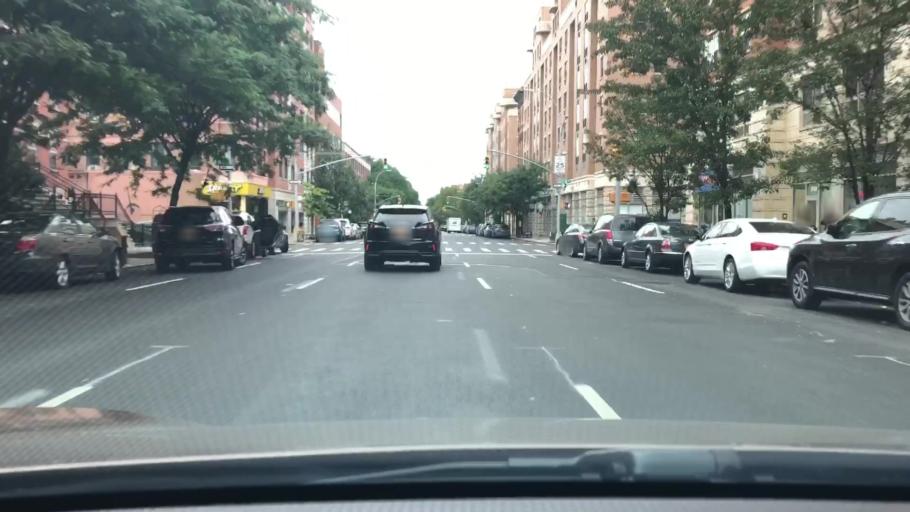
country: US
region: New York
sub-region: New York County
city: Manhattan
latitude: 40.8009
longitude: -73.9442
